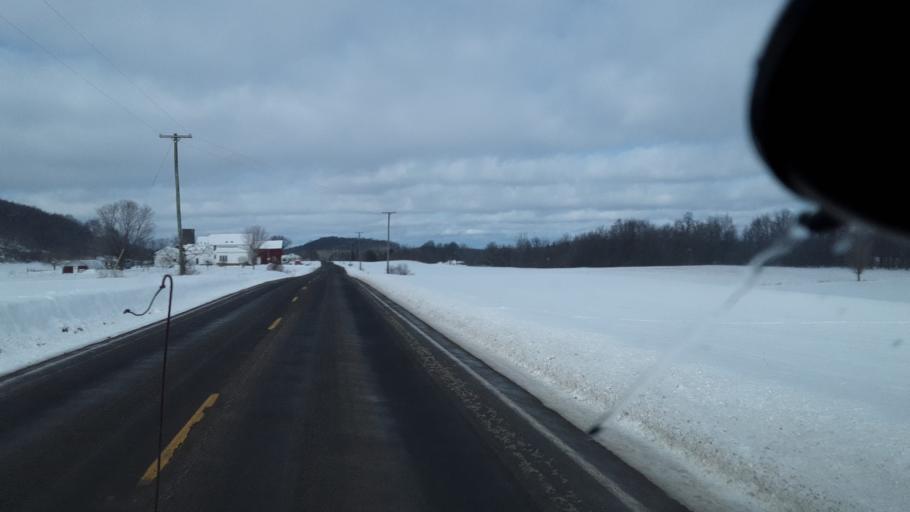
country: US
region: New York
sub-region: Wayne County
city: Newark
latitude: 43.0791
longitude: -77.0573
